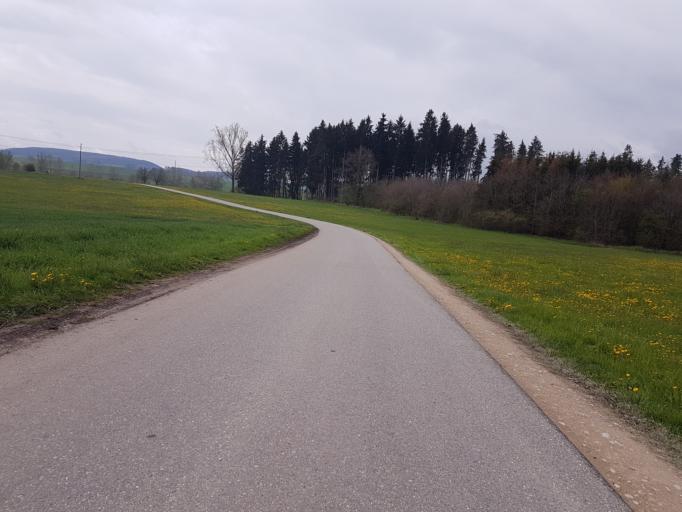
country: DE
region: Baden-Wuerttemberg
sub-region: Freiburg Region
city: Hufingen
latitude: 47.9188
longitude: 8.5167
